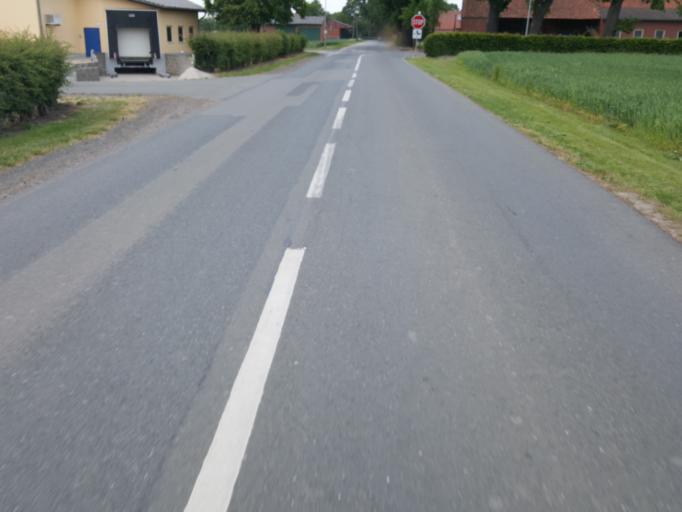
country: DE
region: Lower Saxony
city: Stolzenau
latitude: 52.5162
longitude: 9.0585
